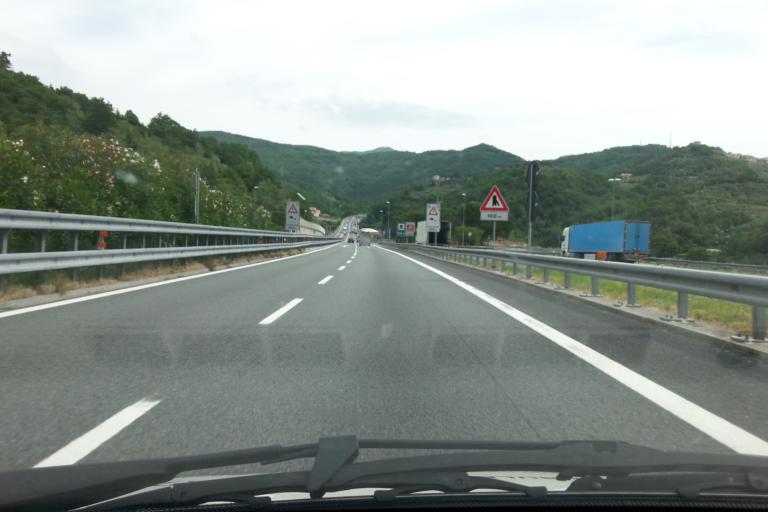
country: IT
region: Liguria
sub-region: Provincia di Savona
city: Feglino
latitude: 44.2124
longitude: 8.3210
